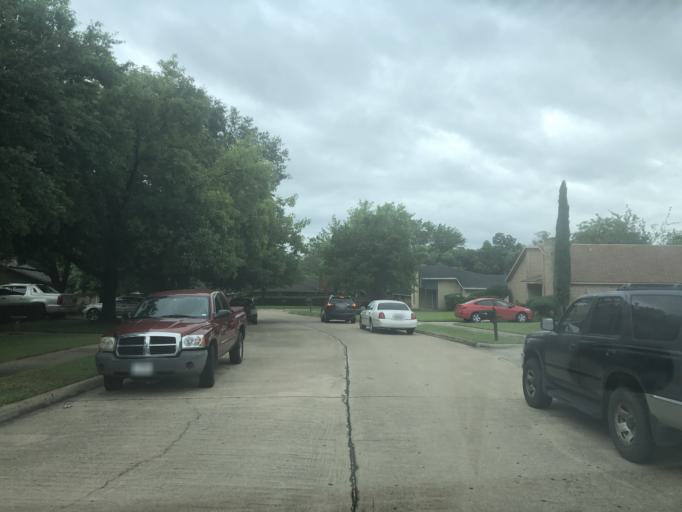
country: US
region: Texas
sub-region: Dallas County
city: Irving
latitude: 32.8010
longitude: -96.9409
